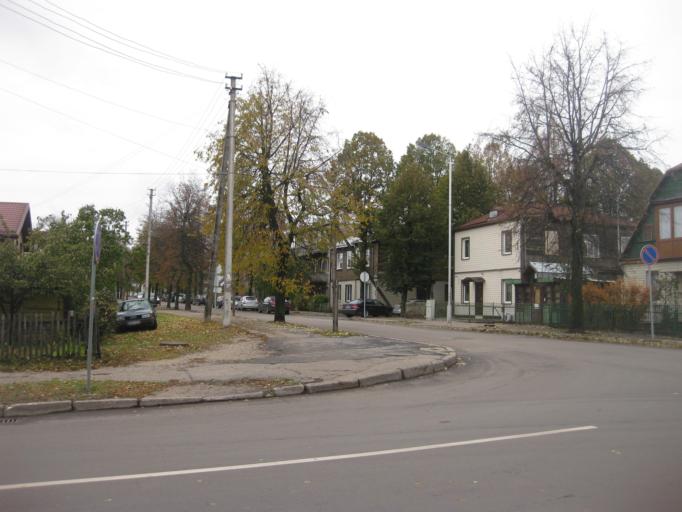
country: LT
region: Kauno apskritis
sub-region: Kaunas
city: Kaunas
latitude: 54.9063
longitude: 23.9197
